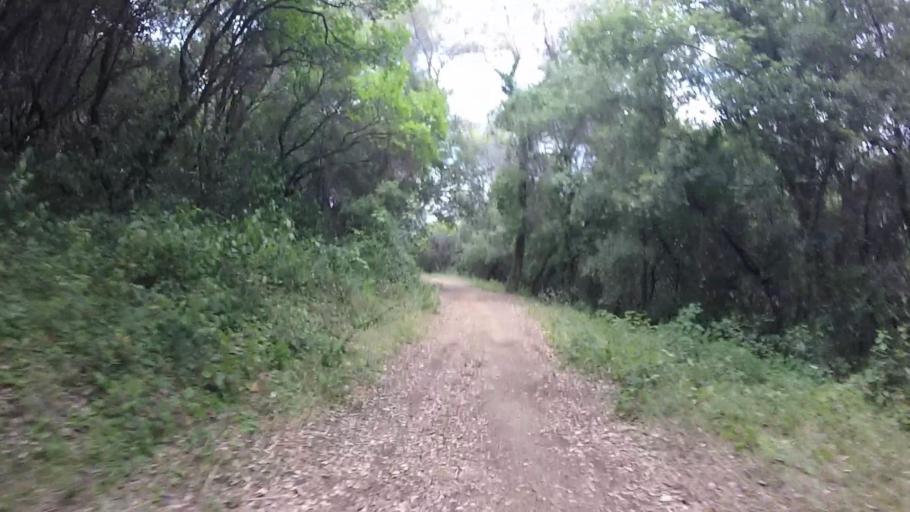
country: FR
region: Provence-Alpes-Cote d'Azur
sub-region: Departement des Alpes-Maritimes
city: Biot
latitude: 43.6157
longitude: 7.0901
